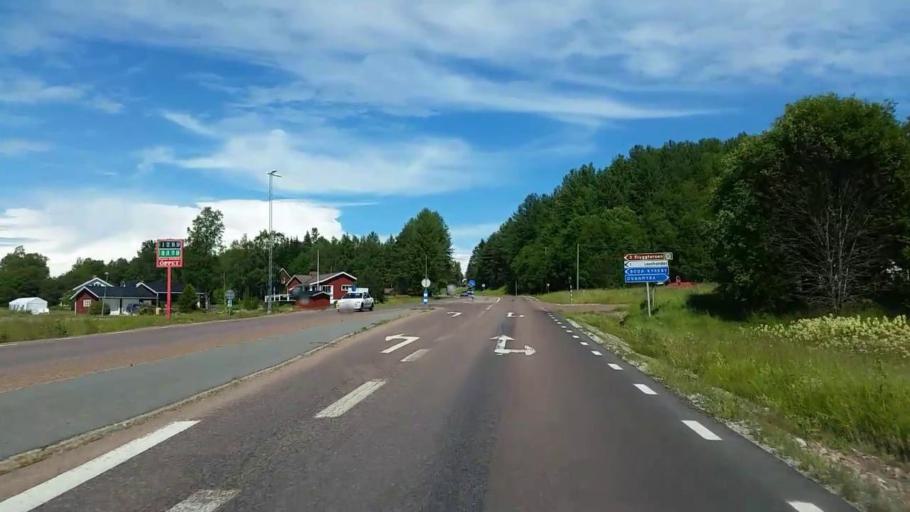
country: SE
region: Dalarna
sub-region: Rattviks Kommun
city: Raettvik
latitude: 61.0038
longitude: 15.2189
